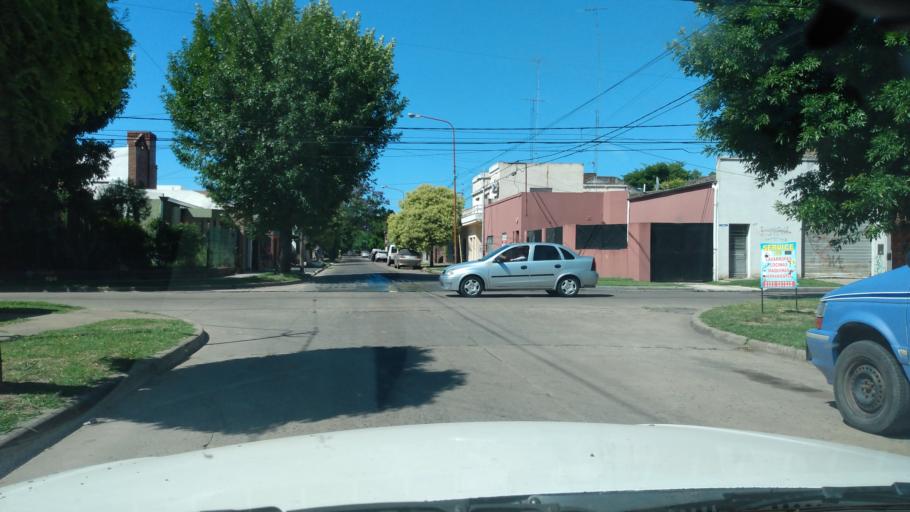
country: AR
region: Buenos Aires
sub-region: Partido de Lujan
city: Lujan
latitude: -34.5627
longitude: -59.1071
